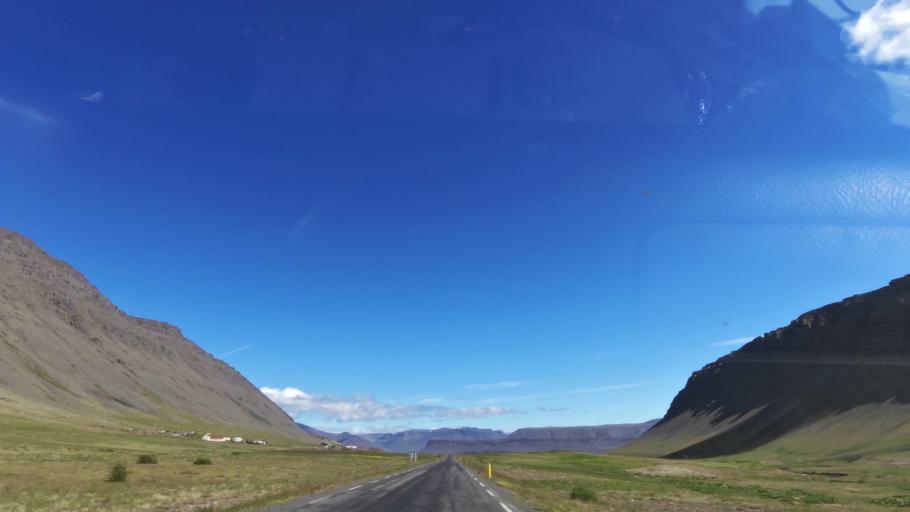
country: IS
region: Westfjords
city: Isafjoerdur
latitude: 65.6682
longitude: -23.6312
